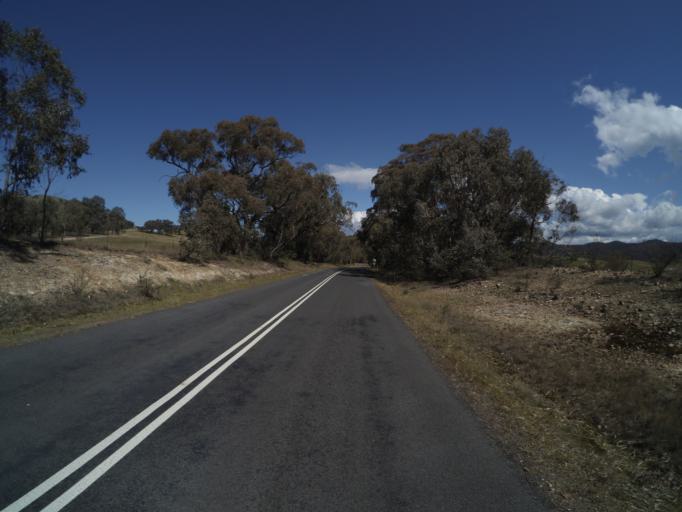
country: AU
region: Australian Capital Territory
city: Macquarie
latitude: -35.1742
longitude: 148.8905
